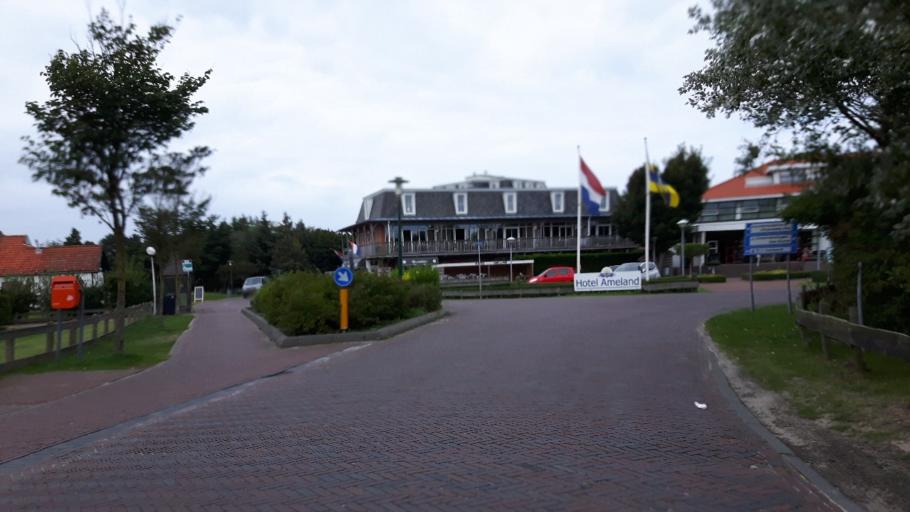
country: NL
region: Friesland
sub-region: Gemeente Ameland
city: Nes
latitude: 53.4516
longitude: 5.7762
